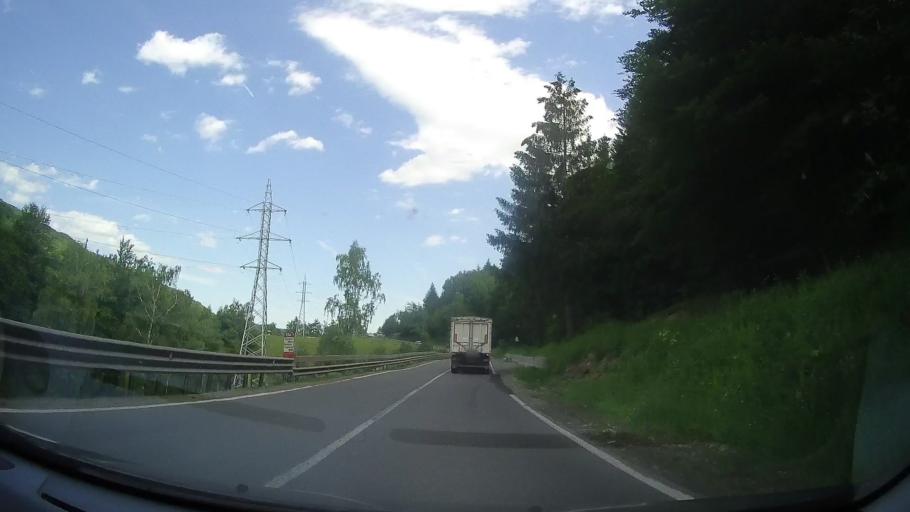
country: RO
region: Prahova
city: Maneciu
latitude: 45.3421
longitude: 25.9532
